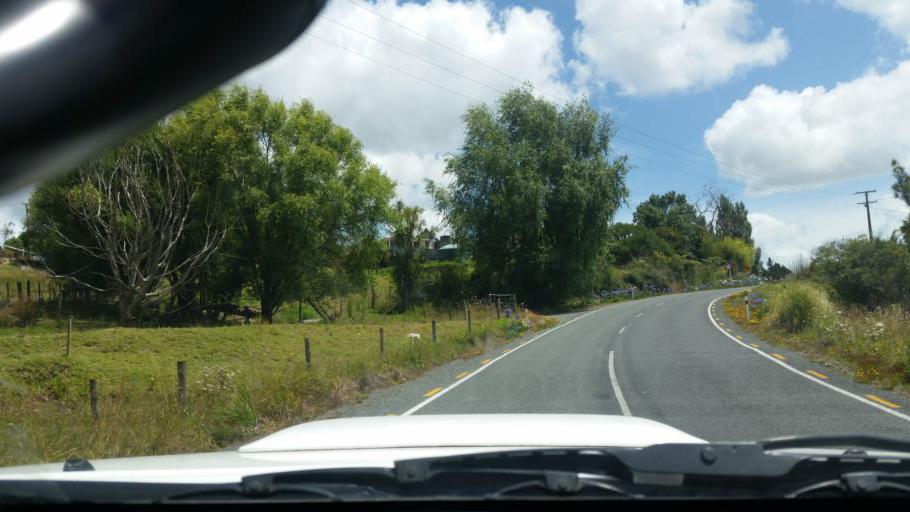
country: NZ
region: Northland
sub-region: Whangarei
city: Ruakaka
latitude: -36.0959
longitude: 174.2426
